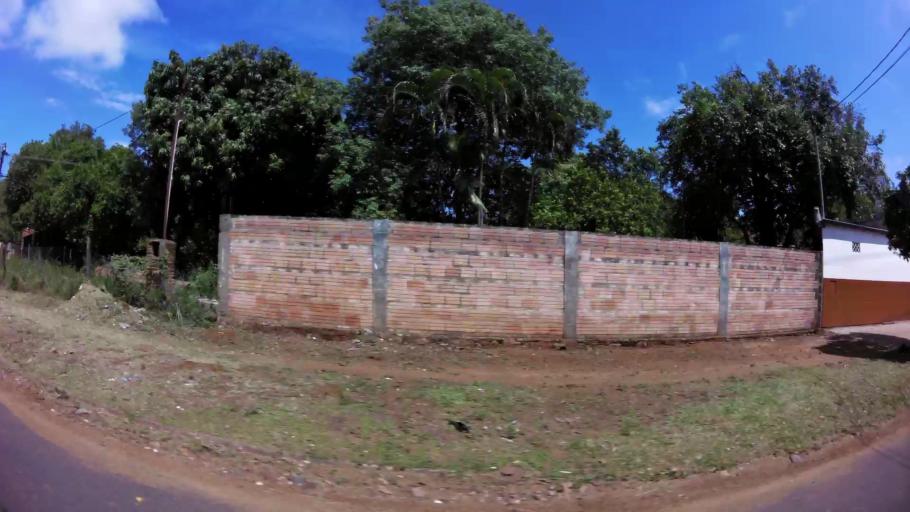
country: PY
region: Central
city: San Lorenzo
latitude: -25.3287
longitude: -57.5098
